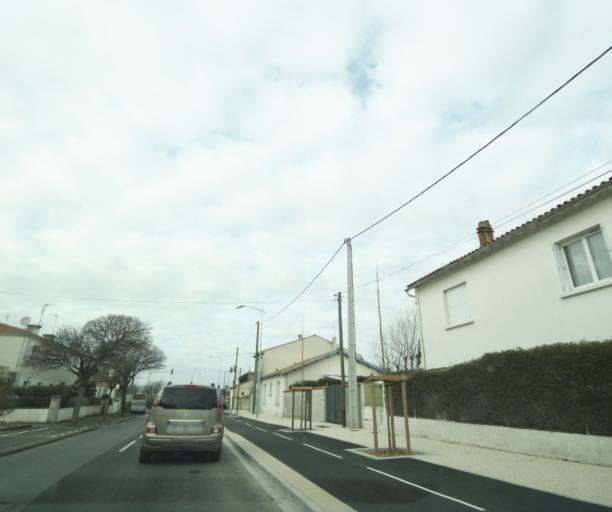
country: FR
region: Poitou-Charentes
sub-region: Departement de la Charente-Maritime
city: La Rochelle
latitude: 46.1710
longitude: -1.1643
